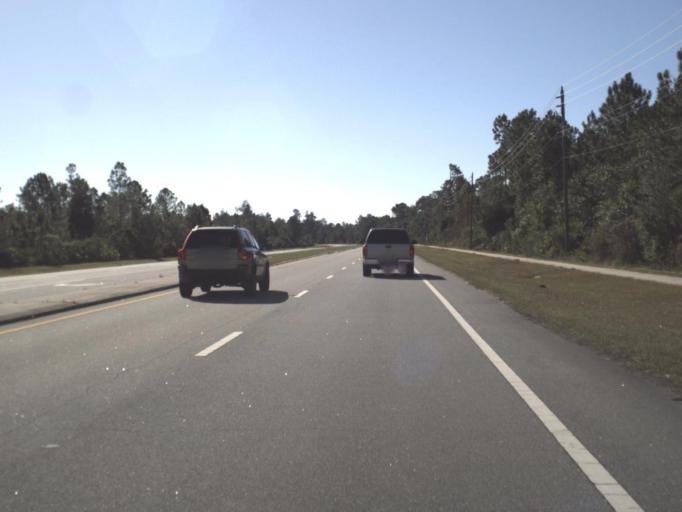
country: US
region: Florida
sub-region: Volusia County
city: Ormond Beach
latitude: 29.2496
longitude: -81.0939
